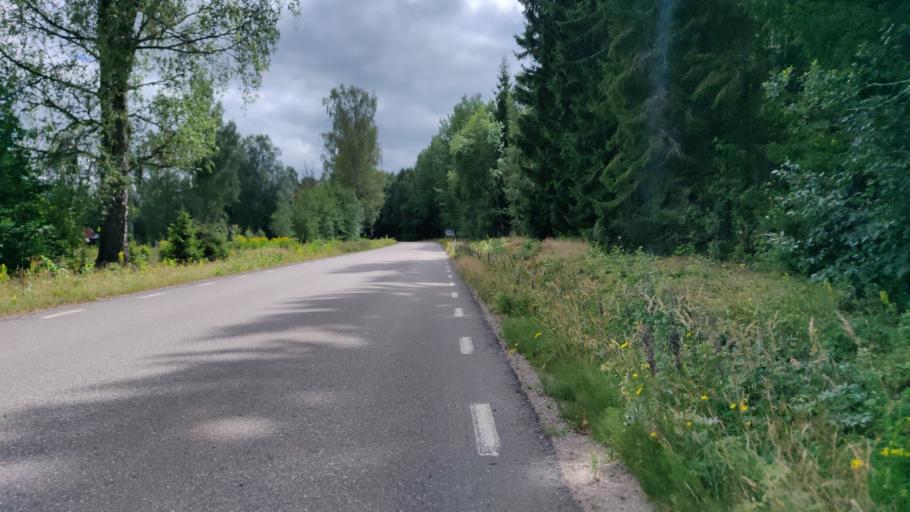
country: SE
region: Vaermland
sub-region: Hagfors Kommun
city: Hagfors
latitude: 59.9859
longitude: 13.6062
